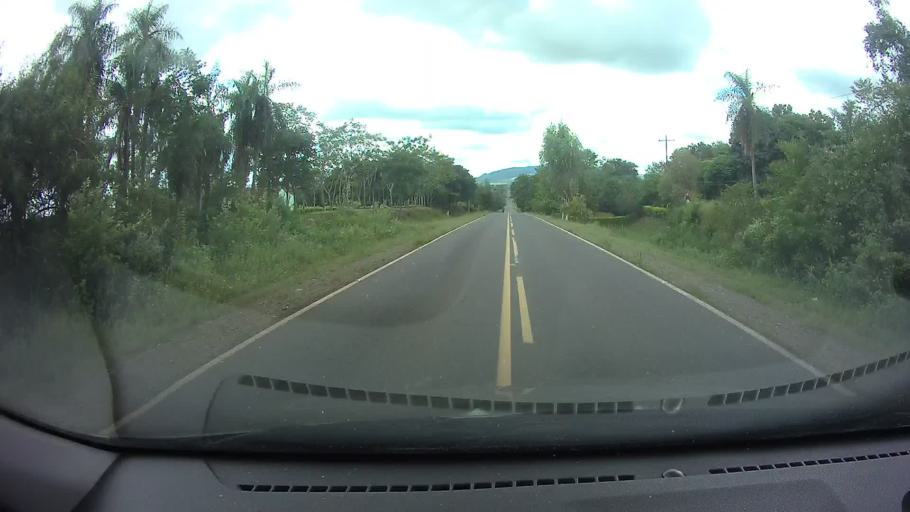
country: PY
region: Paraguari
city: Acahay
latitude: -25.9130
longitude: -57.0505
